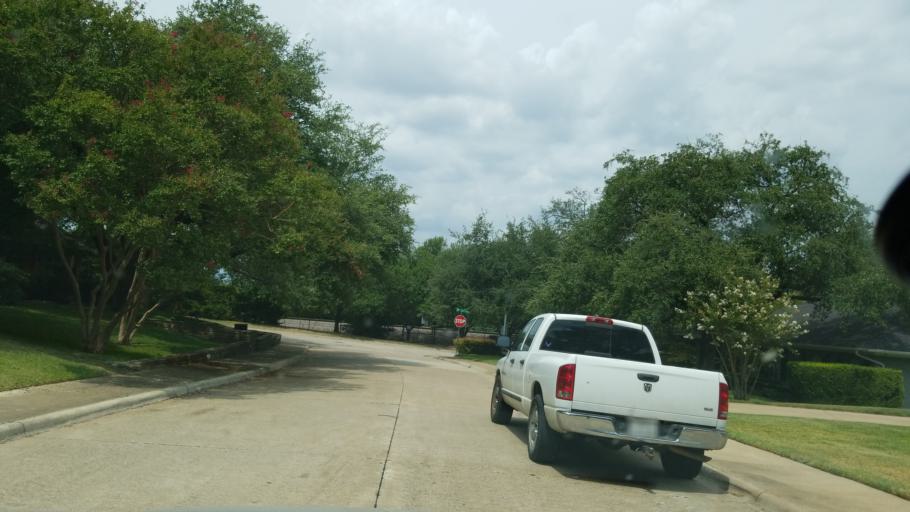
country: US
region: Texas
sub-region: Dallas County
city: Richardson
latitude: 32.8916
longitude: -96.7242
